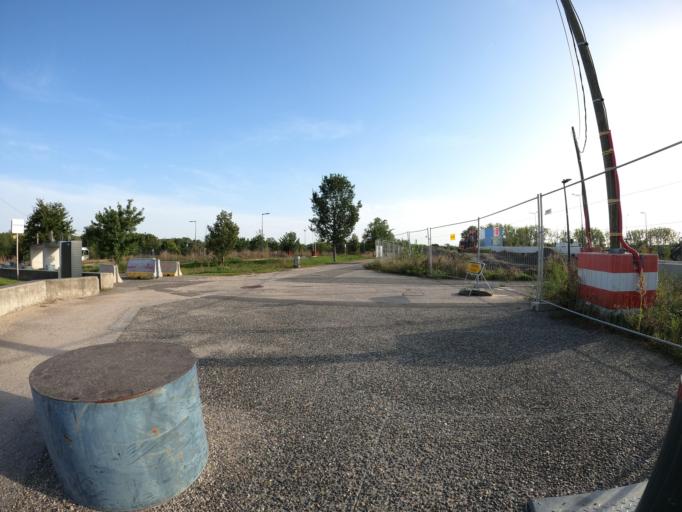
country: FR
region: Midi-Pyrenees
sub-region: Departement de la Haute-Garonne
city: Vieille-Toulouse
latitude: 43.5546
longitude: 1.4313
